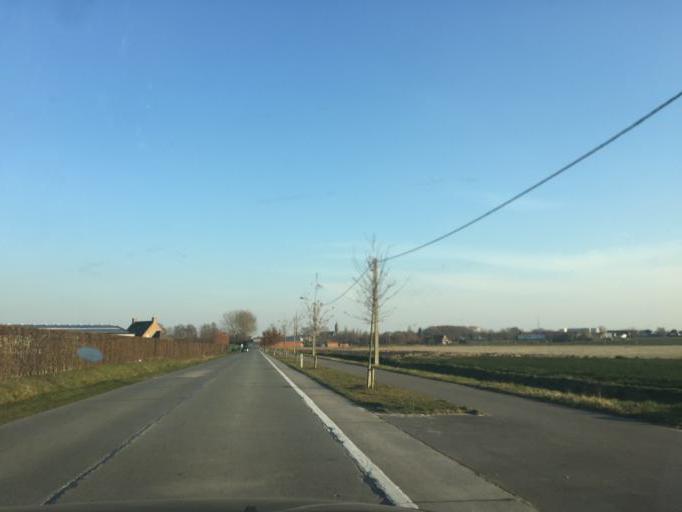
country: BE
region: Flanders
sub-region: Provincie West-Vlaanderen
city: Oostrozebeke
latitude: 50.9279
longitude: 3.3174
